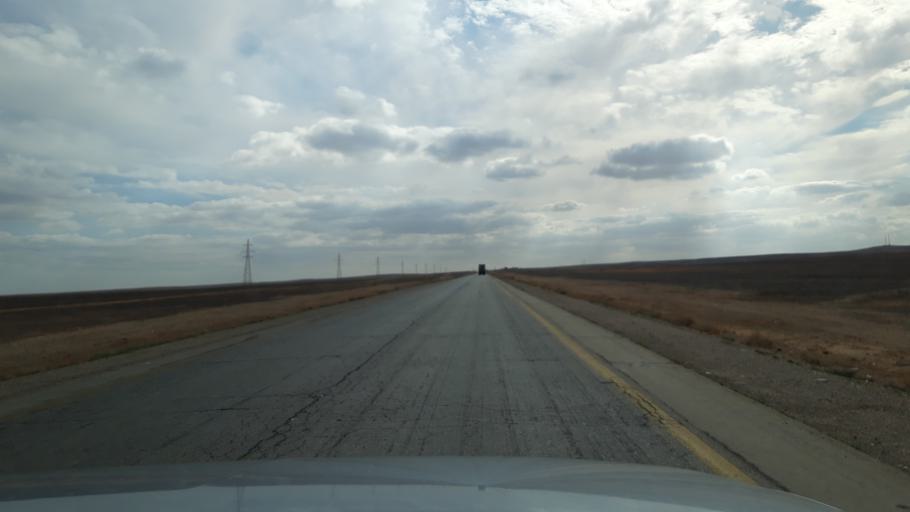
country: JO
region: Amman
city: Al Azraq ash Shamali
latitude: 31.7632
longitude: 36.5555
